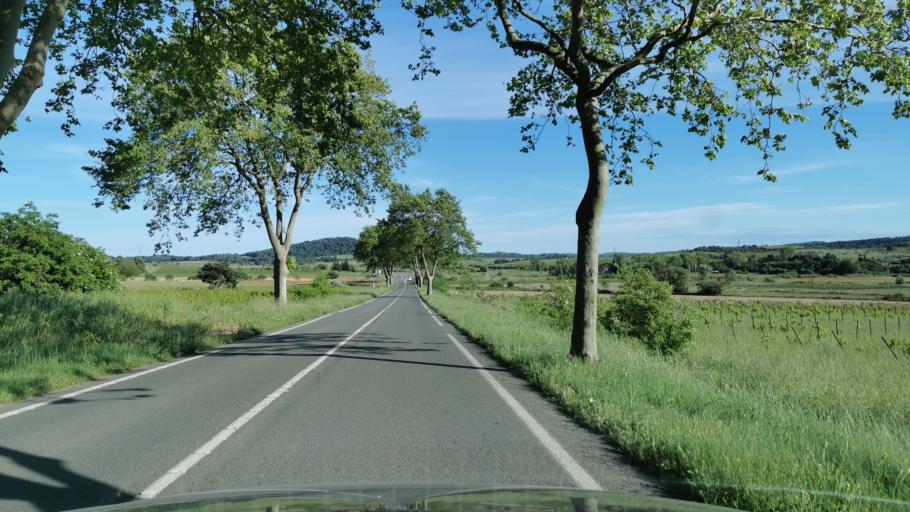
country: FR
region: Languedoc-Roussillon
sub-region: Departement de l'Aude
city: Marcorignan
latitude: 43.2208
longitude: 2.9259
